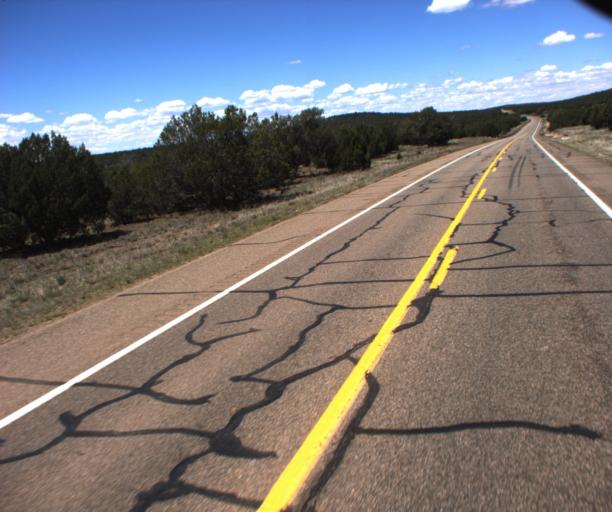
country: US
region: Arizona
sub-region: Yavapai County
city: Paulden
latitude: 35.1186
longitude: -112.4337
